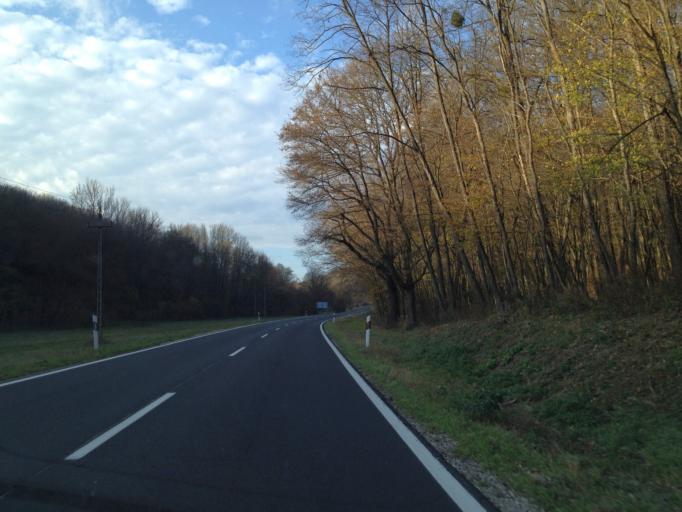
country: HU
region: Gyor-Moson-Sopron
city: Bakonyszentlaszlo
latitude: 47.3973
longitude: 17.8585
